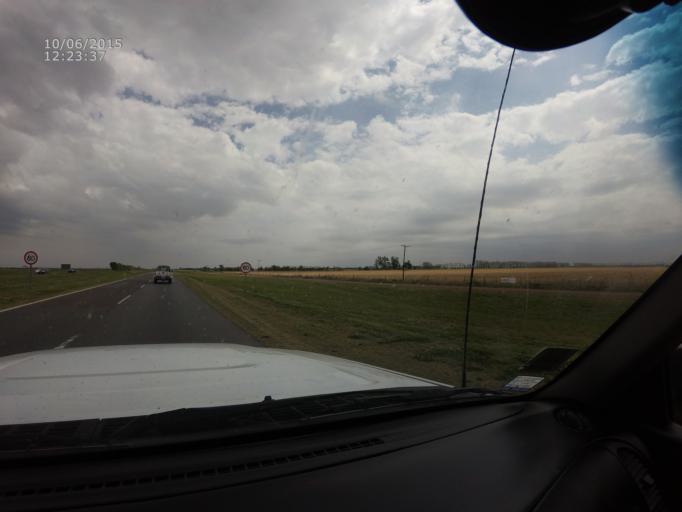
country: AR
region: Santa Fe
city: Roldan
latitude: -32.9134
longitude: -60.9613
